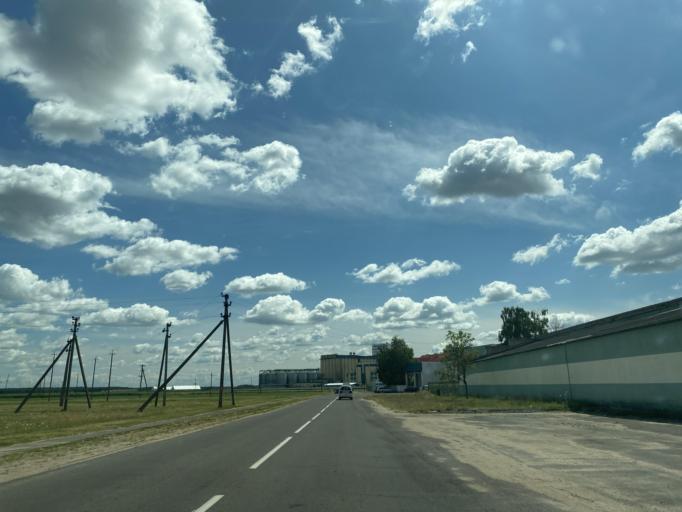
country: BY
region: Brest
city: Ivanava
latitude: 52.1412
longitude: 25.5489
